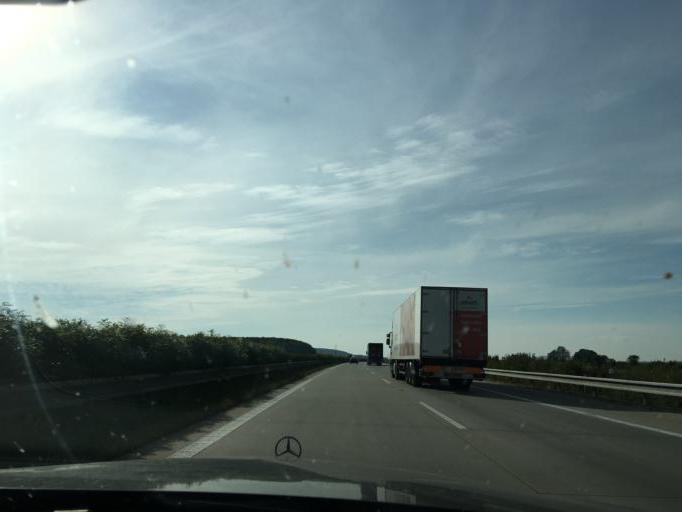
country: CZ
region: Central Bohemia
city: Zizelice
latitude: 50.1292
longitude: 15.3446
